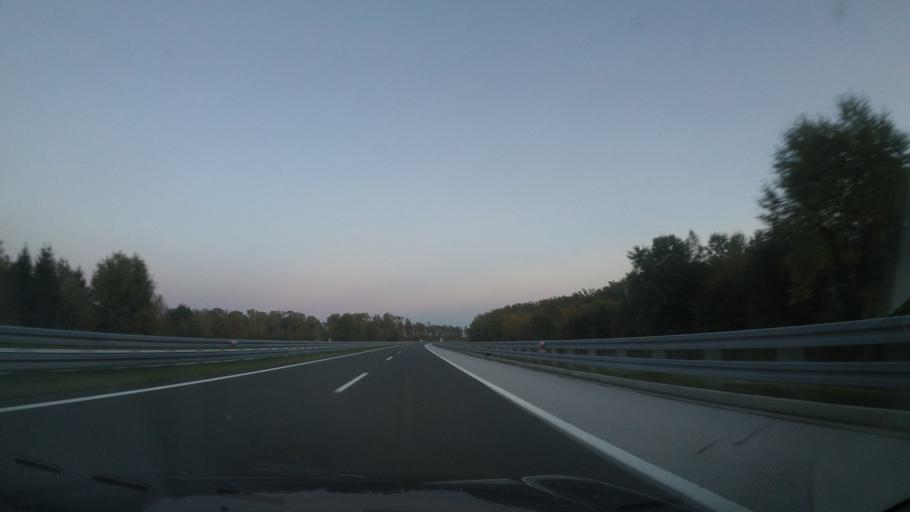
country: HR
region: Sisacko-Moslavacka
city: Lekenik
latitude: 45.5869
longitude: 16.1795
